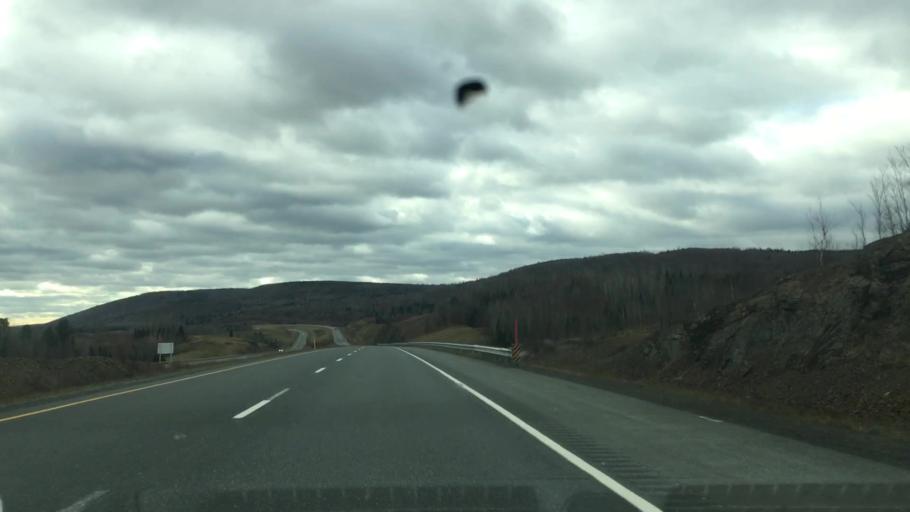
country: US
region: Maine
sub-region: Aroostook County
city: Fort Fairfield
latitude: 46.7136
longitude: -67.7350
